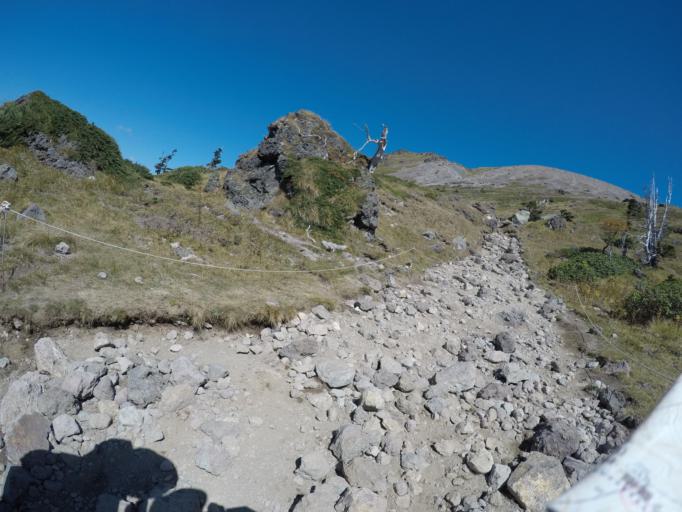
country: JP
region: Tochigi
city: Nikko
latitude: 36.7948
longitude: 139.3731
